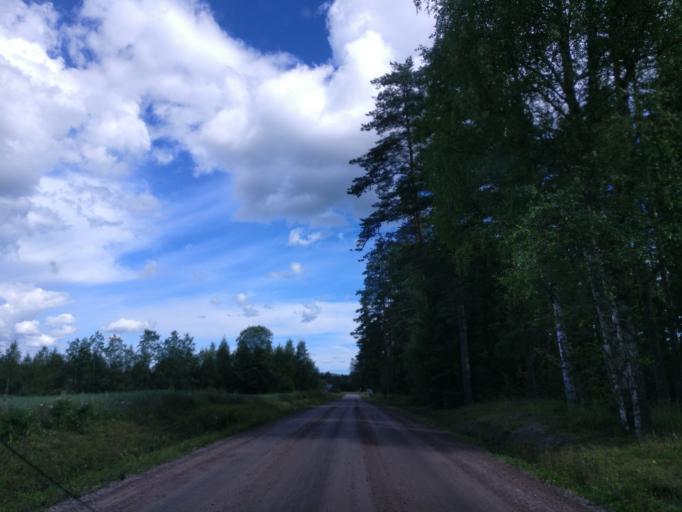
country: SE
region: Vaermland
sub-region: Hagfors Kommun
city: Ekshaerad
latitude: 60.0587
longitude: 13.4780
